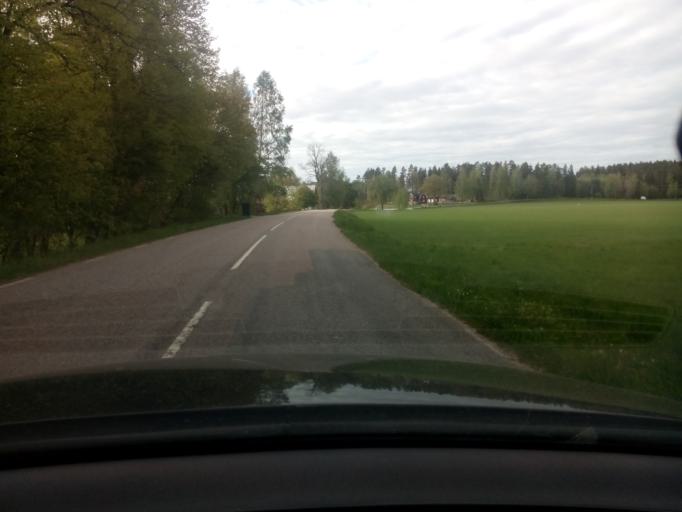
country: SE
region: Soedermanland
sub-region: Nykopings Kommun
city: Nykoping
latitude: 58.8433
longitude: 16.9317
